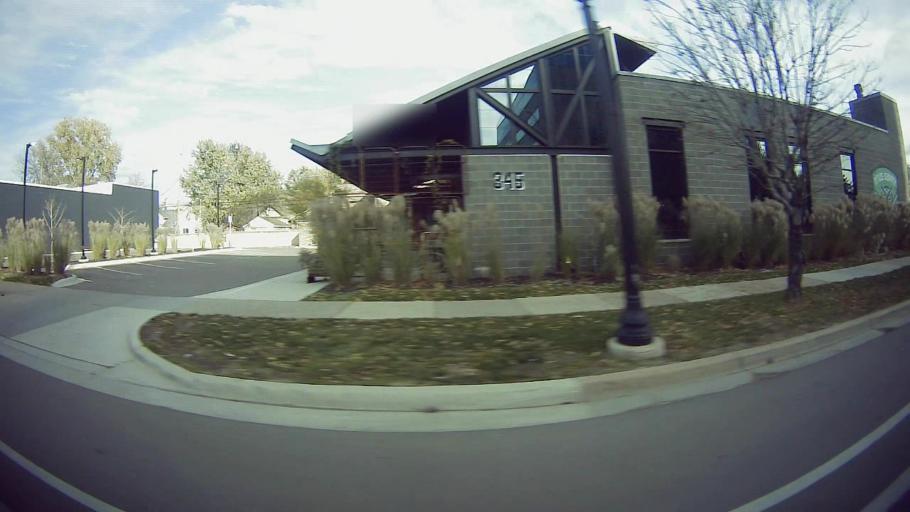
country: US
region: Michigan
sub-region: Oakland County
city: Ferndale
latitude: 42.4607
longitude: -83.1302
